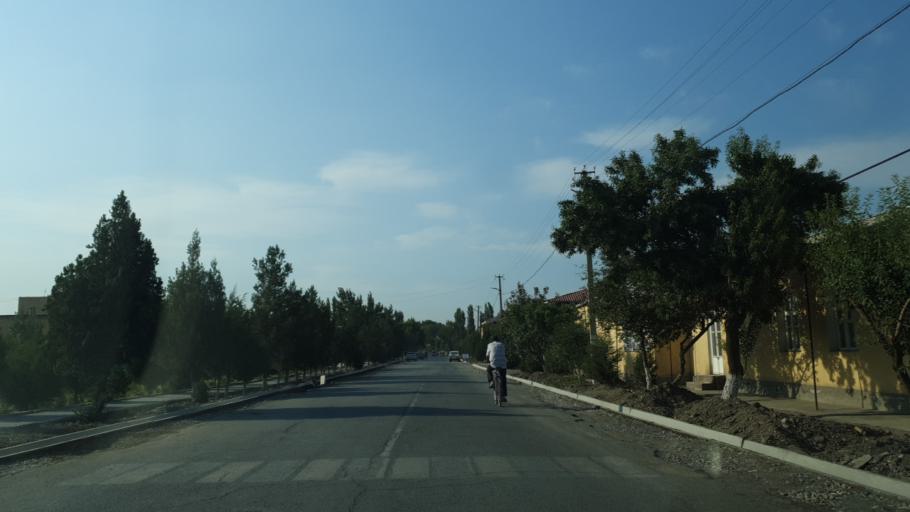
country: UZ
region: Fergana
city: Yaypan
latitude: 40.3739
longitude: 70.8126
